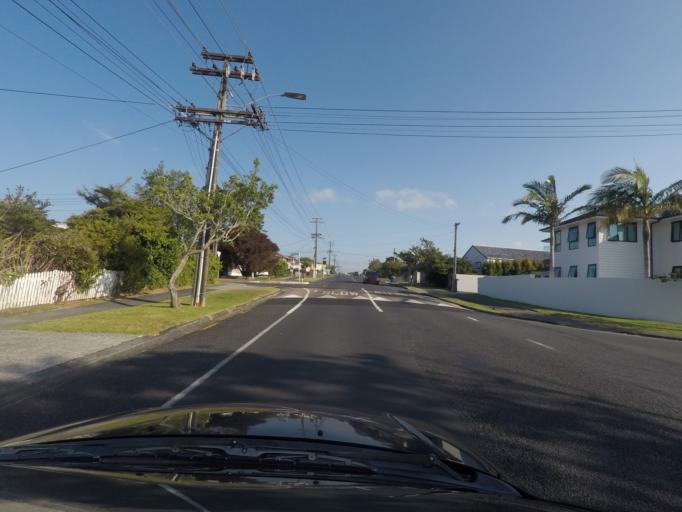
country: NZ
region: Auckland
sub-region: Auckland
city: Rosebank
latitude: -36.8579
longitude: 174.6431
